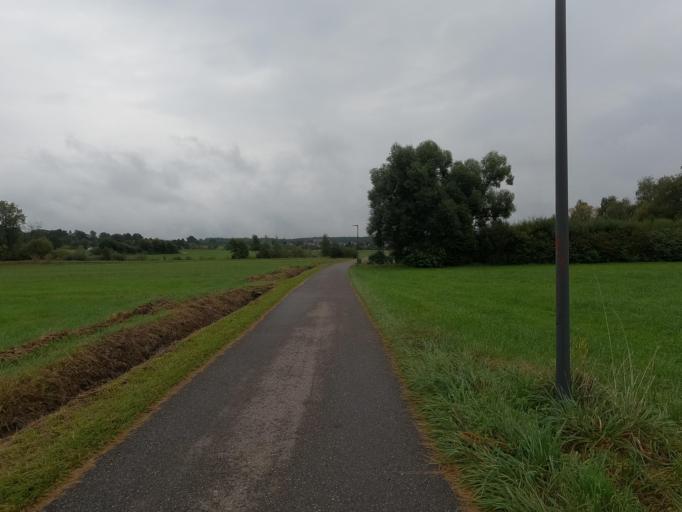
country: DE
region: Baden-Wuerttemberg
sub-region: Freiburg Region
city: Radolfzell am Bodensee
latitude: 47.7453
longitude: 8.9890
